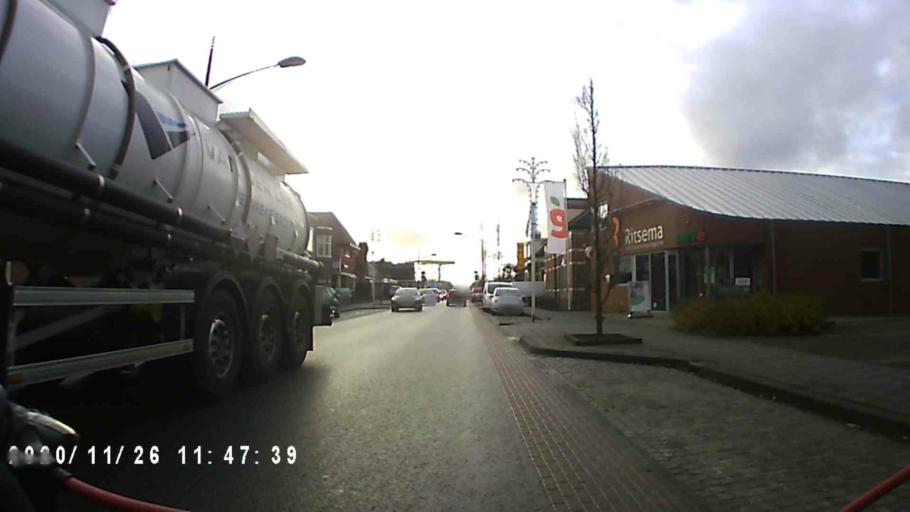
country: NL
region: Groningen
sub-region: Gemeente Bedum
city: Bedum
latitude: 53.3017
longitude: 6.5962
